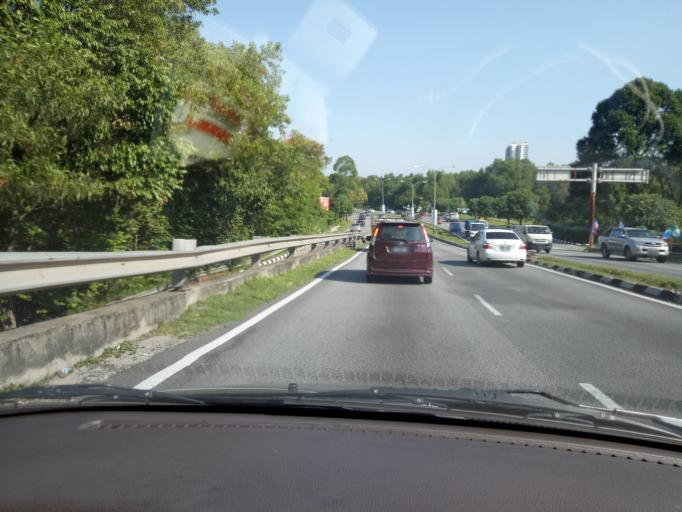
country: MY
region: Selangor
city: Kampong Baharu Balakong
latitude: 3.0104
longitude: 101.7991
